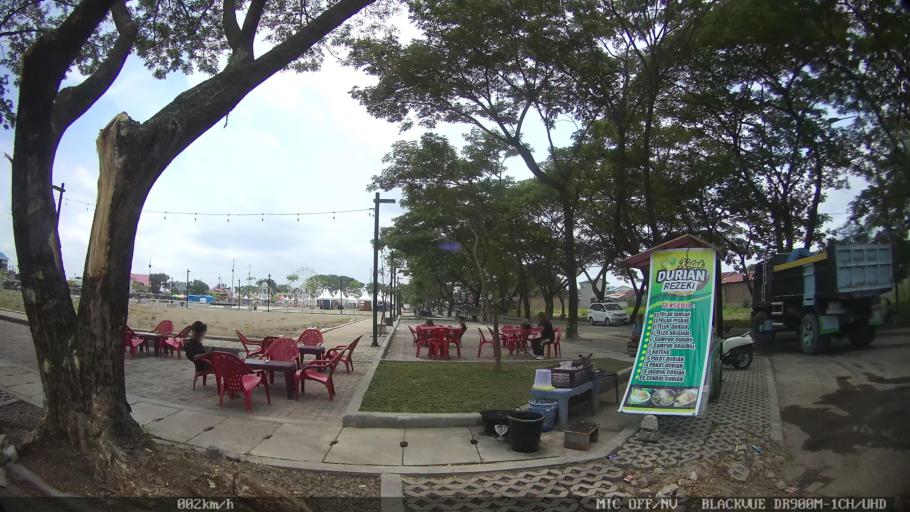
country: ID
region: North Sumatra
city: Labuhan Deli
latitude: 3.6936
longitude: 98.6948
